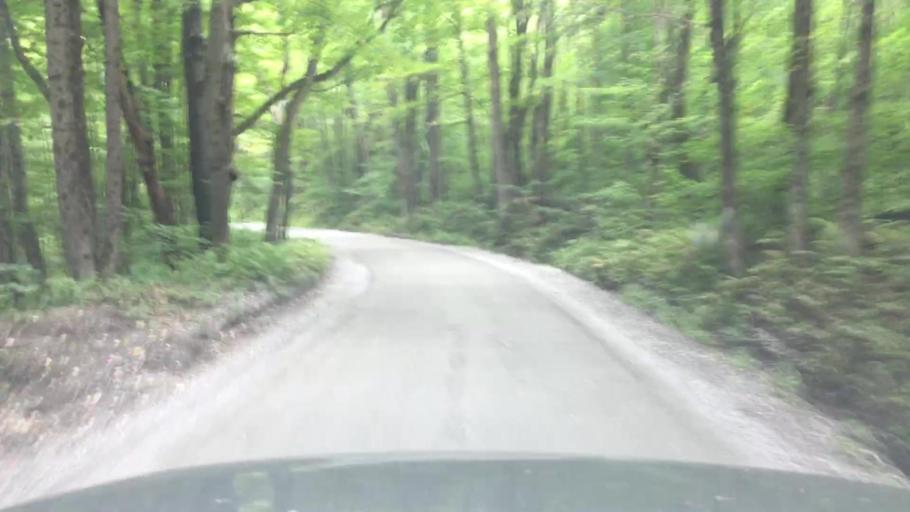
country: US
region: Vermont
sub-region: Windham County
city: Dover
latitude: 42.8488
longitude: -72.7742
